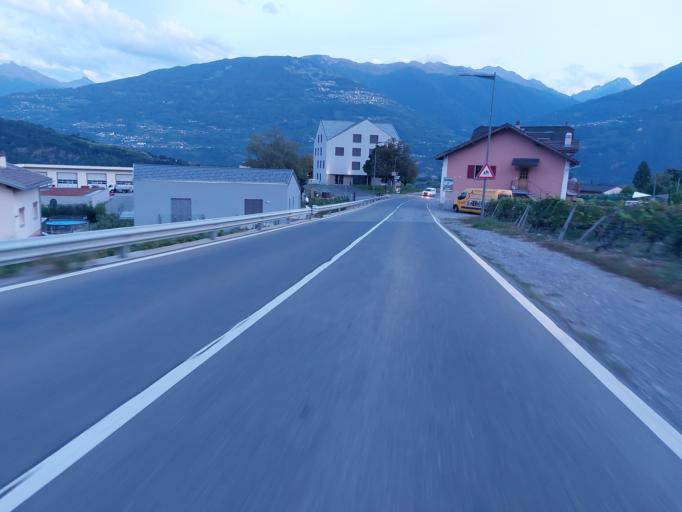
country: CH
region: Valais
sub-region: Conthey District
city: Conthey
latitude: 46.2356
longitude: 7.3046
